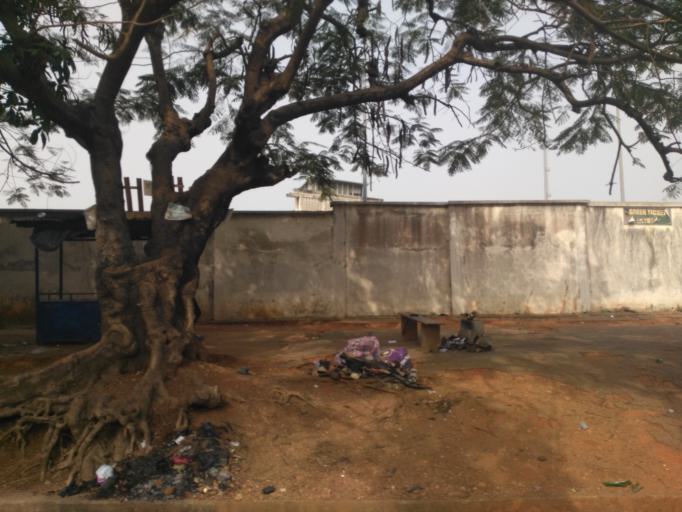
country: GH
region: Ashanti
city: Kumasi
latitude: 6.6808
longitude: -1.6054
